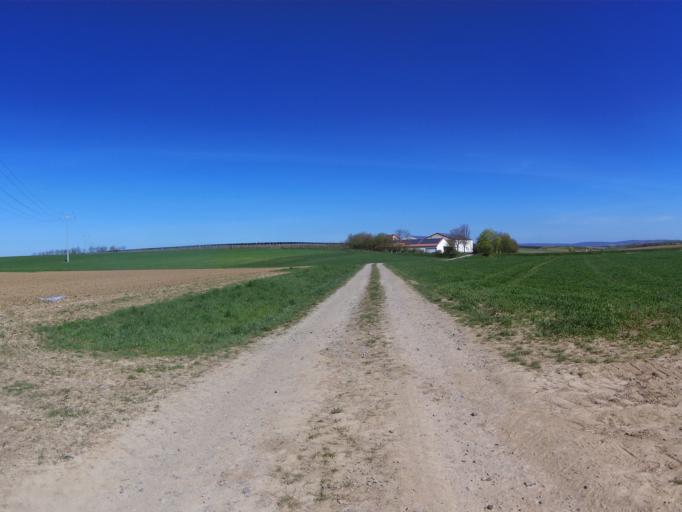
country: DE
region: Bavaria
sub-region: Regierungsbezirk Unterfranken
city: Biebelried
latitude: 49.8066
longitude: 10.1011
